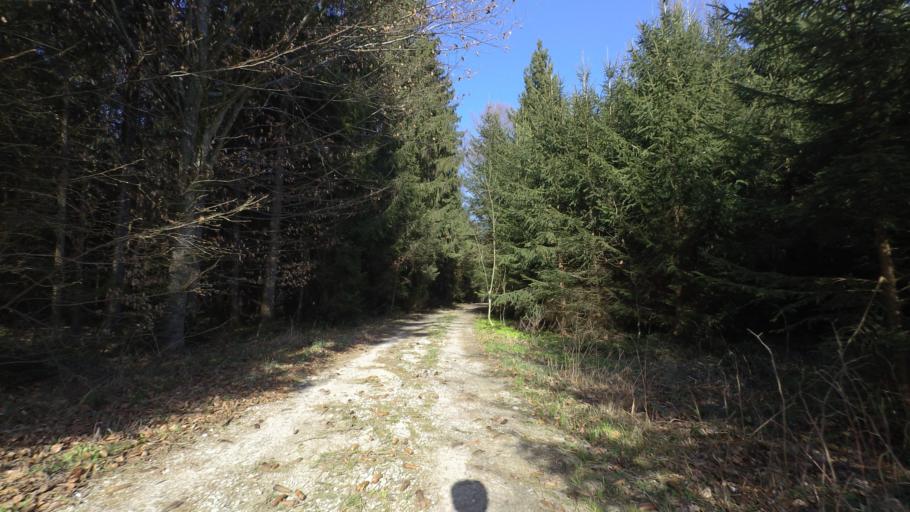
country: DE
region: Bavaria
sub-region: Upper Bavaria
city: Nussdorf
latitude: 47.9185
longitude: 12.6020
